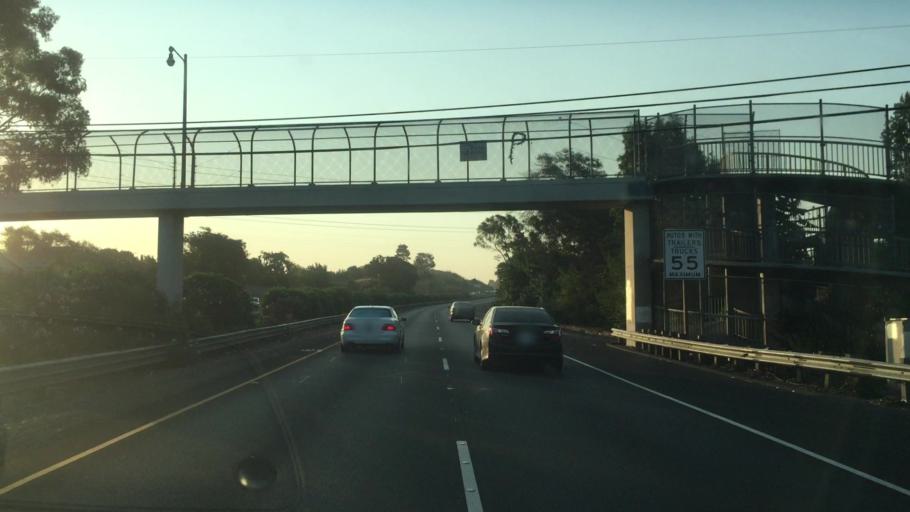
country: US
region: California
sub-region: Contra Costa County
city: Crockett
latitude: 38.0891
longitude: -122.2216
